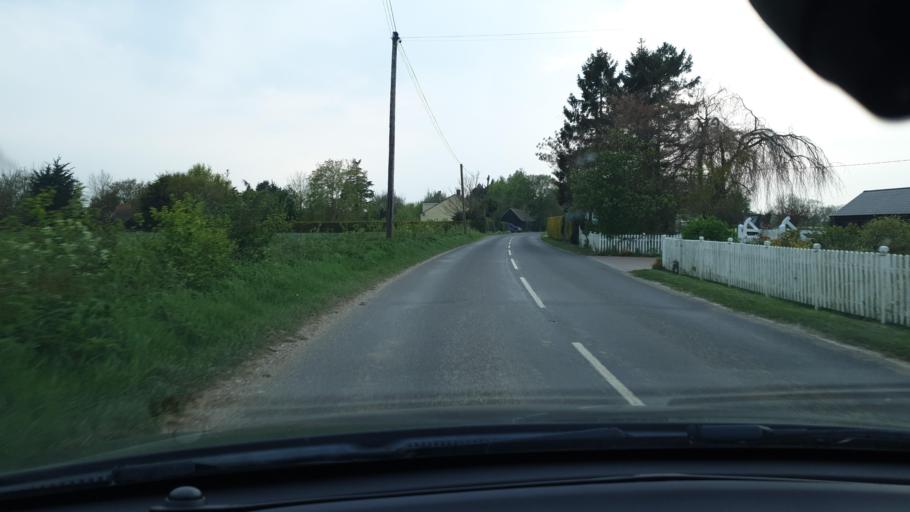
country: GB
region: England
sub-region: Essex
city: Mistley
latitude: 51.9051
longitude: 1.1084
